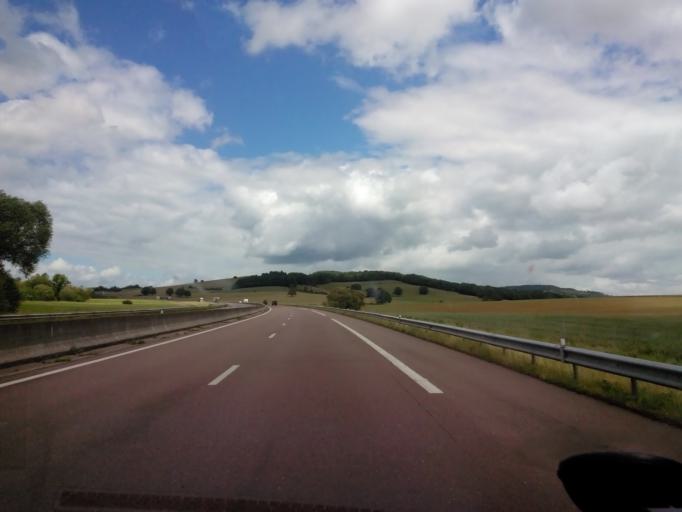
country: FR
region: Lorraine
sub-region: Departement des Vosges
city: Chatenois
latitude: 48.3537
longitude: 5.8616
